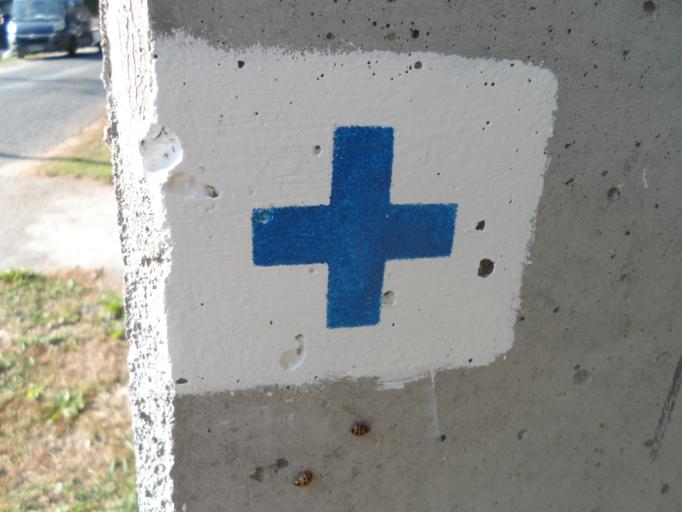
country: HU
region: Veszprem
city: Urkut
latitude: 47.2173
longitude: 17.6409
